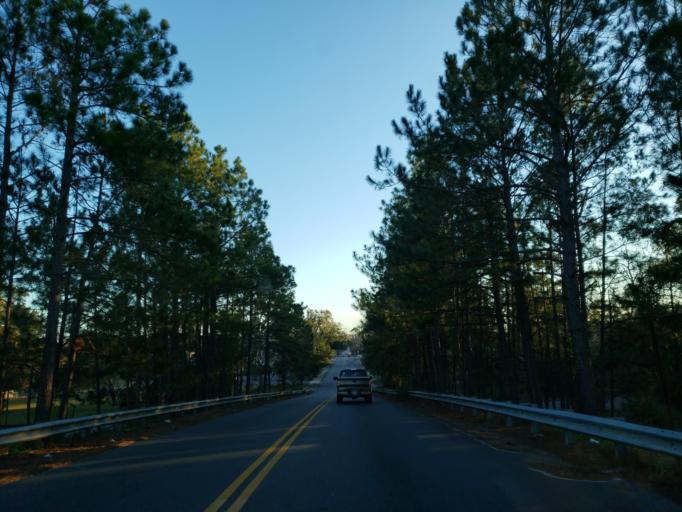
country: US
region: Georgia
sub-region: Crisp County
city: Cordele
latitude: 31.9698
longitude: -83.7796
